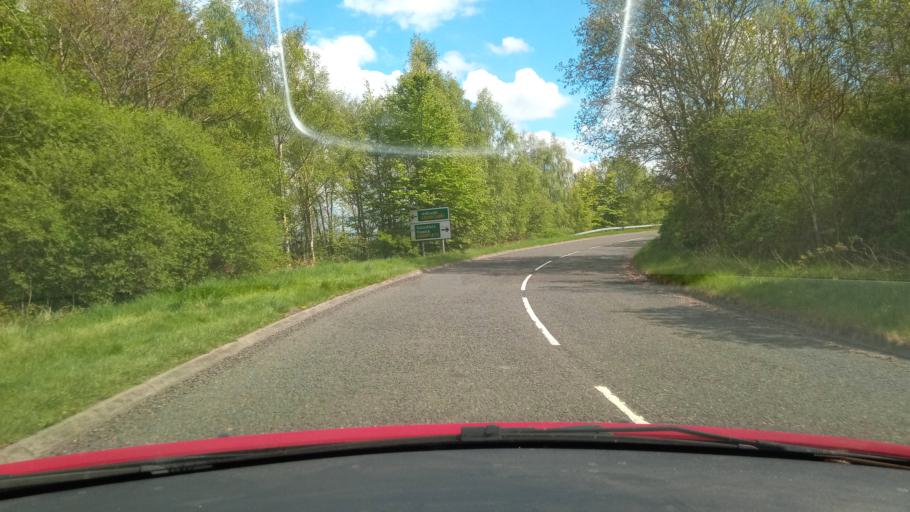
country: GB
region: Scotland
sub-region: The Scottish Borders
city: Newtown St Boswells
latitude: 55.5998
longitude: -2.6893
